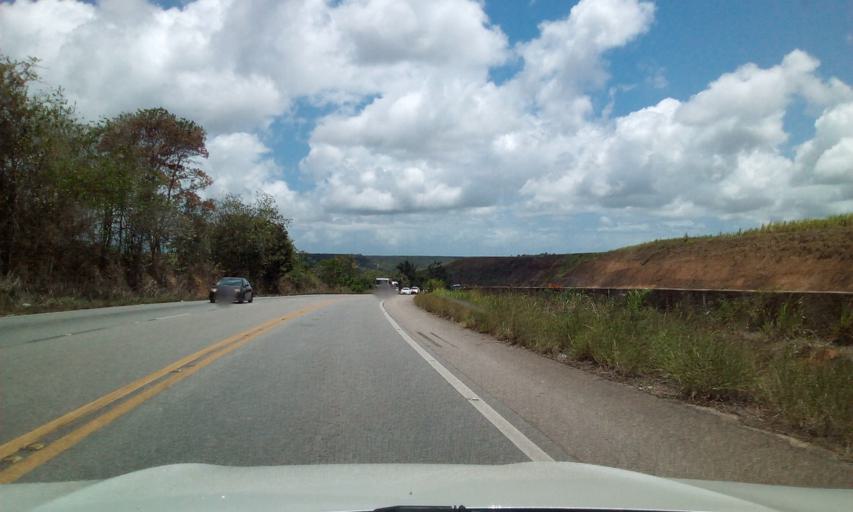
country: BR
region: Alagoas
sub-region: Sao Miguel Dos Campos
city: Sao Miguel dos Campos
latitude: -9.8903
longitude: -36.1556
